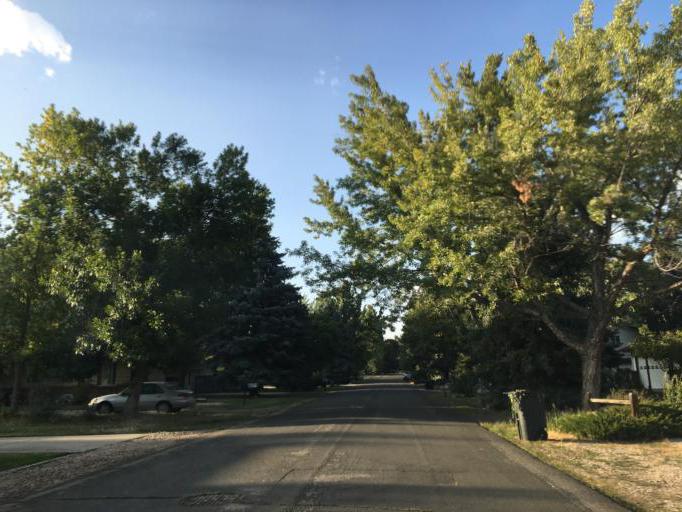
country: US
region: Colorado
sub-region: Jefferson County
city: Applewood
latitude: 39.7912
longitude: -105.1636
